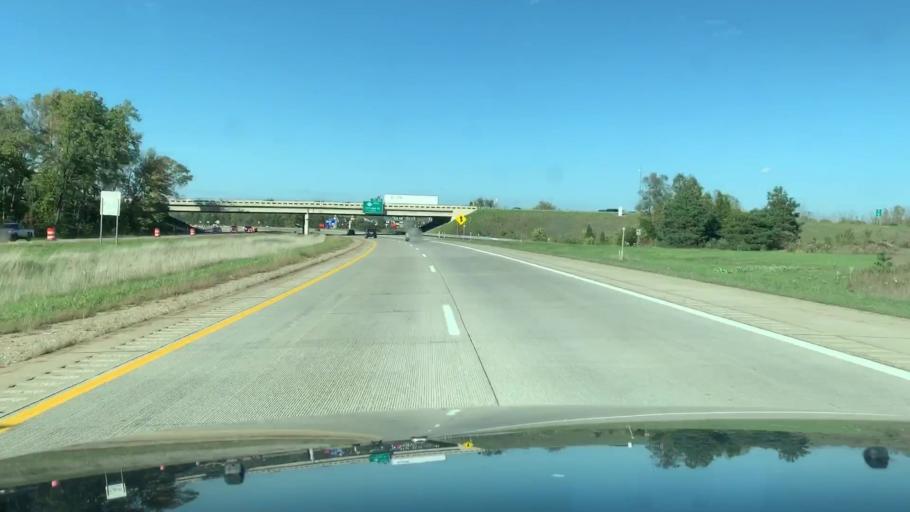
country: US
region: Michigan
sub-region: Ottawa County
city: Jenison
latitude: 42.8832
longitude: -85.7774
